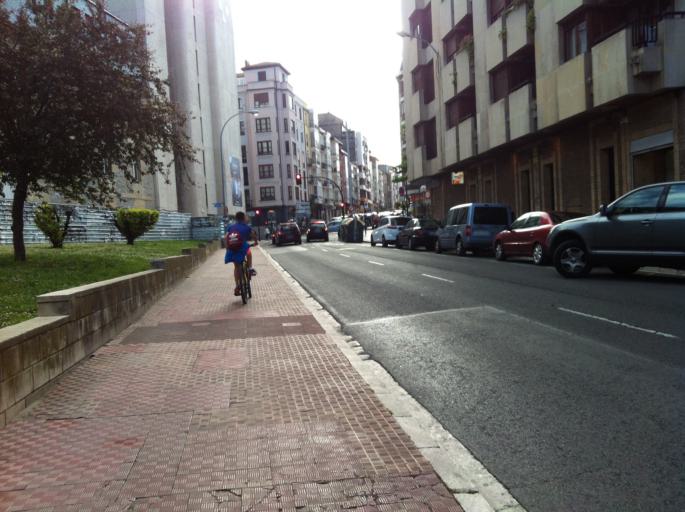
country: ES
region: Basque Country
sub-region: Provincia de Alava
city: Gasteiz / Vitoria
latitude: 42.8470
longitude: -2.6668
